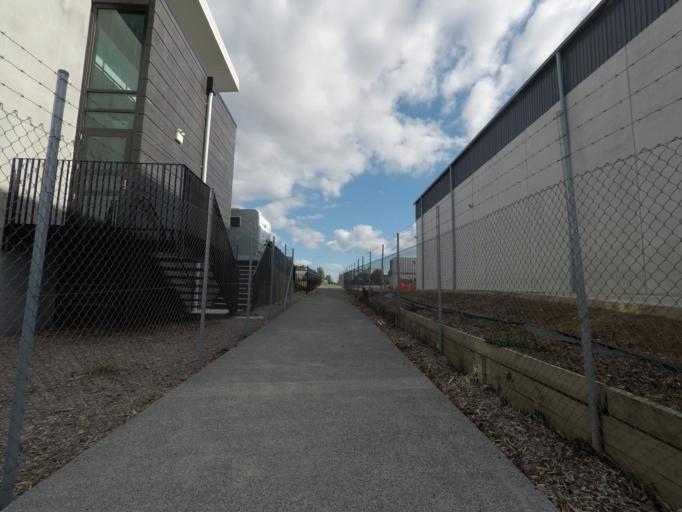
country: NZ
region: Auckland
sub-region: Auckland
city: Rosebank
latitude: -36.8813
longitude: 174.6844
